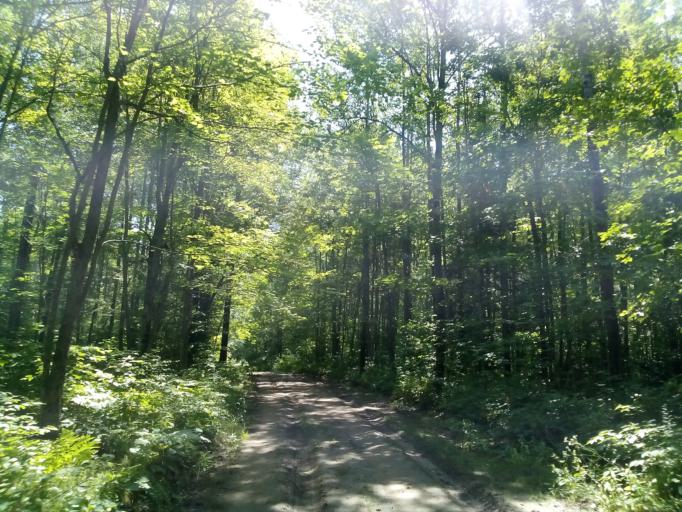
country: US
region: Wisconsin
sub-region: Forest County
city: Crandon
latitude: 45.3655
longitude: -88.5228
